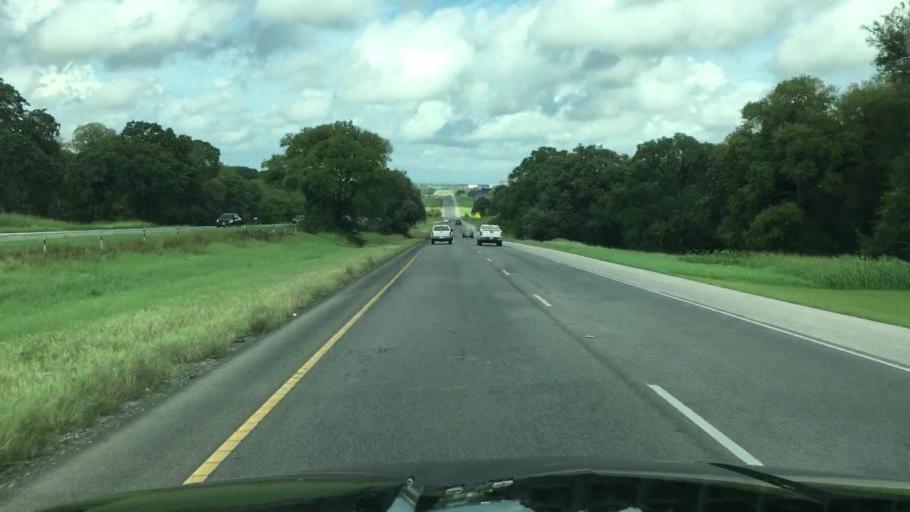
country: US
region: Texas
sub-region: Bastrop County
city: Wyldwood
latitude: 30.1536
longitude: -97.4918
